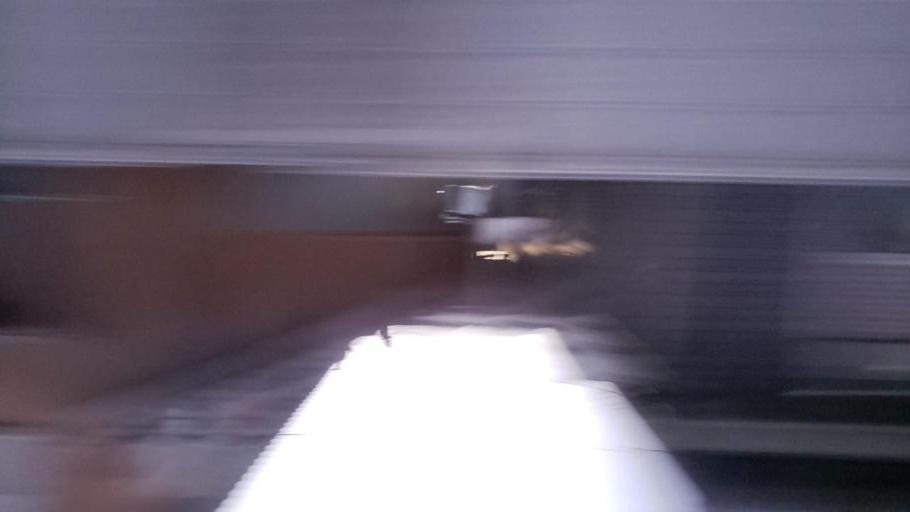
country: JP
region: Tokushima
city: Kamojimacho-jogejima
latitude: 34.1010
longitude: 134.3055
